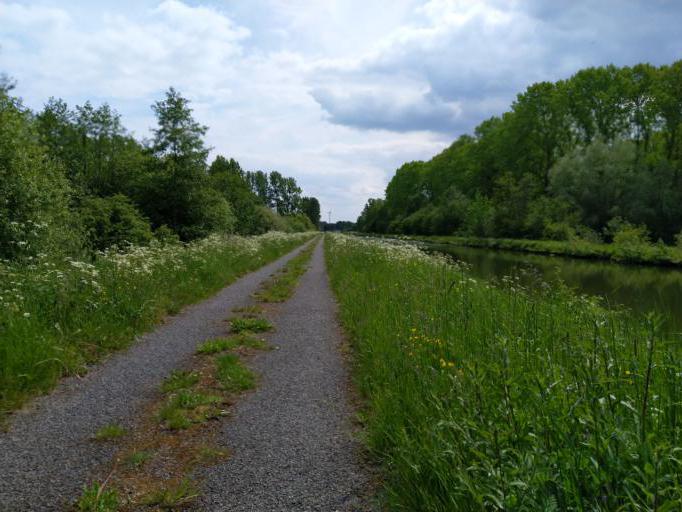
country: FR
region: Picardie
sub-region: Departement de l'Aisne
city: Wassigny
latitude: 50.0549
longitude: 3.6430
